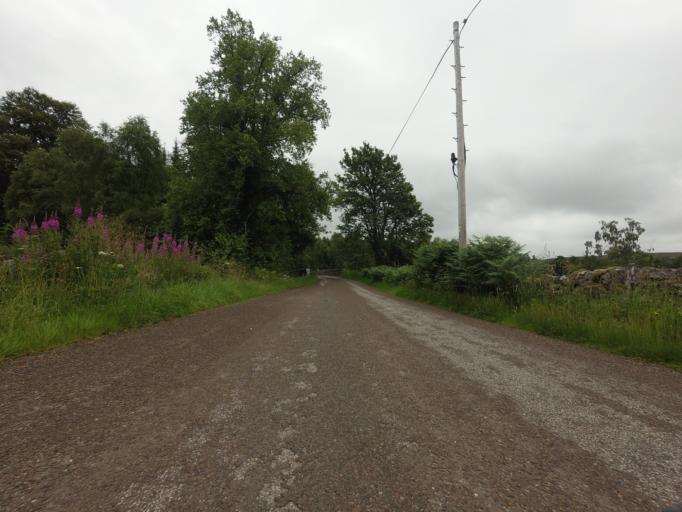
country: GB
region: Scotland
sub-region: Highland
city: Evanton
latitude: 57.9842
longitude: -4.4190
